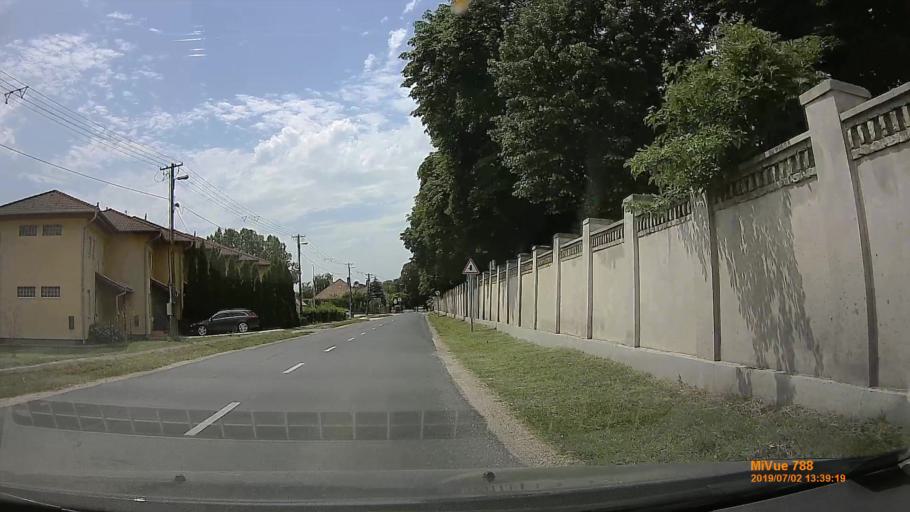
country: HU
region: Gyor-Moson-Sopron
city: Mosonmagyarovar
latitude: 47.8570
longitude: 17.2831
